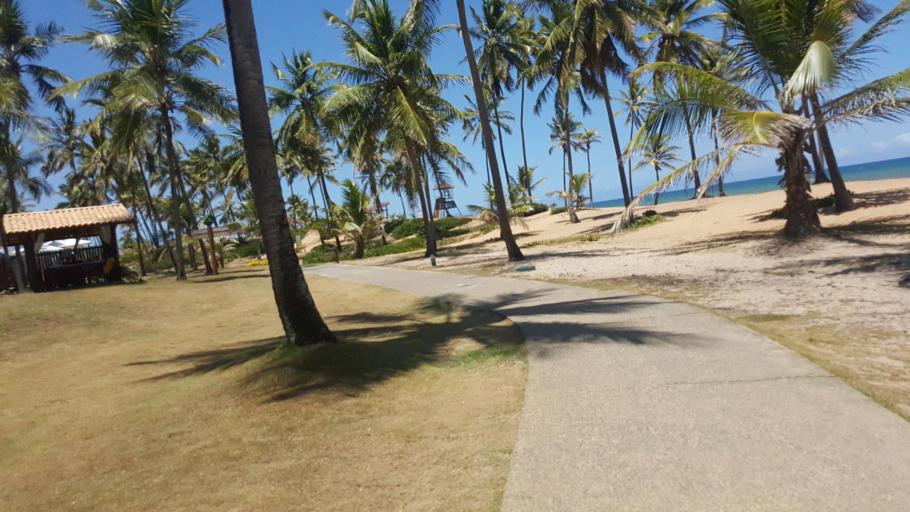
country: BR
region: Bahia
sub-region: Mata De Sao Joao
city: Mata de Sao Joao
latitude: -12.4406
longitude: -37.9180
